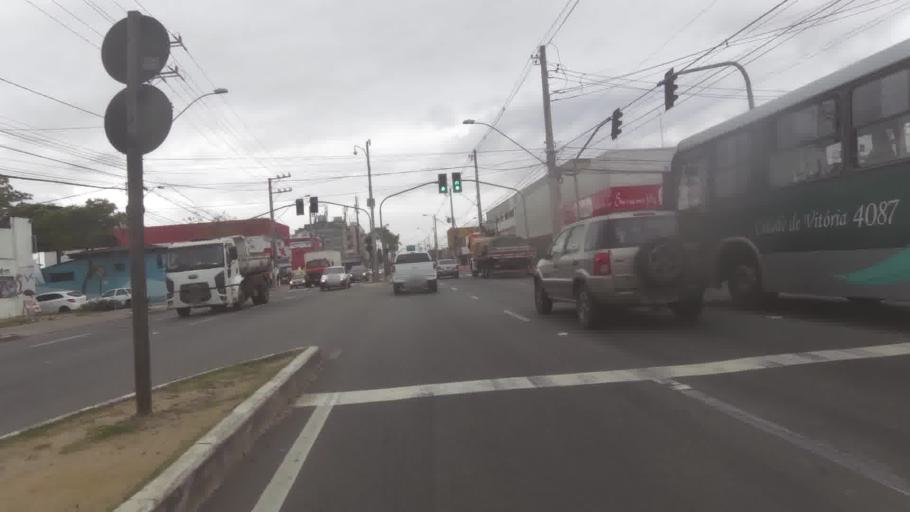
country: BR
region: Espirito Santo
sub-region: Vila Velha
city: Vila Velha
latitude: -20.2680
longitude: -40.2992
